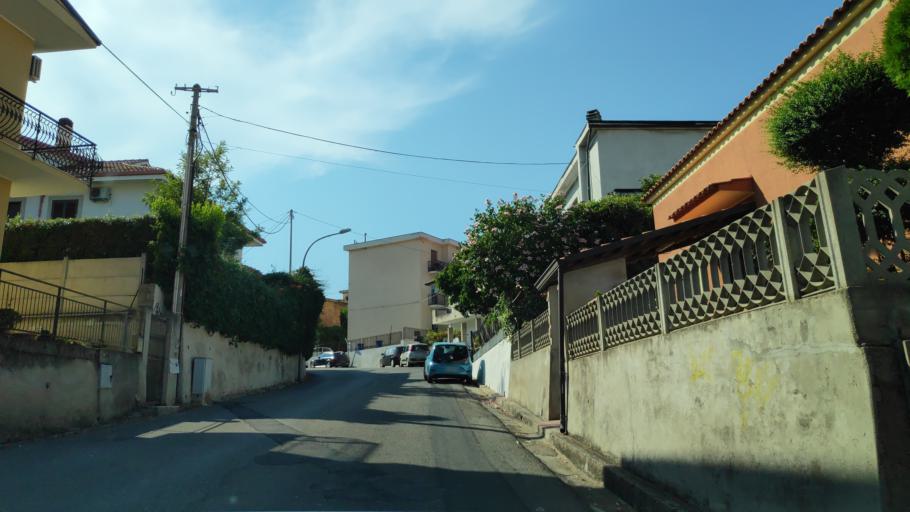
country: IT
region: Calabria
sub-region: Provincia di Catanzaro
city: Soverato Superiore
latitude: 38.6896
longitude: 16.5334
